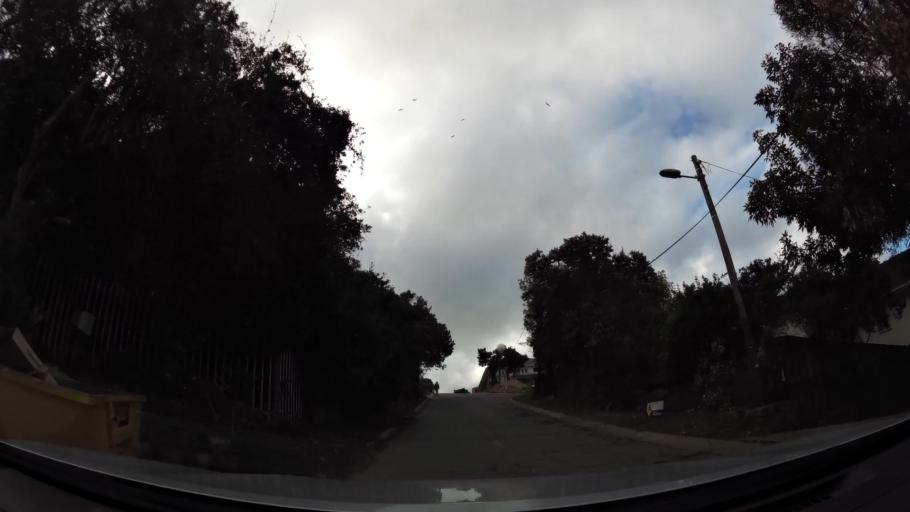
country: ZA
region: Western Cape
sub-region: Eden District Municipality
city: Plettenberg Bay
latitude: -34.0586
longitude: 23.3769
